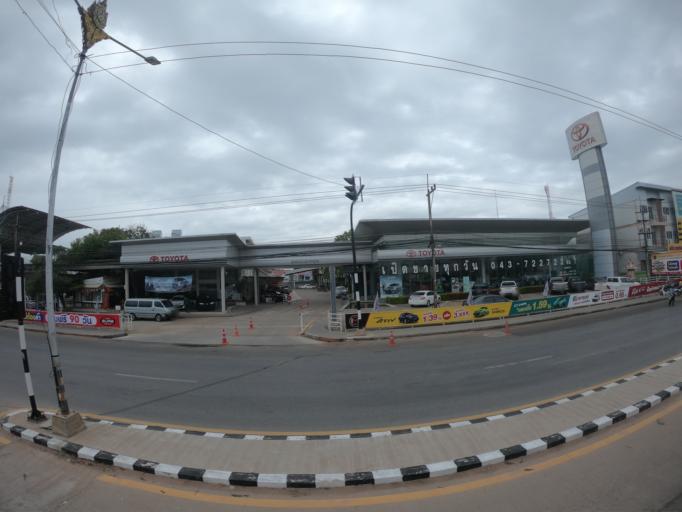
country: TH
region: Maha Sarakham
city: Maha Sarakham
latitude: 16.1779
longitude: 103.2974
